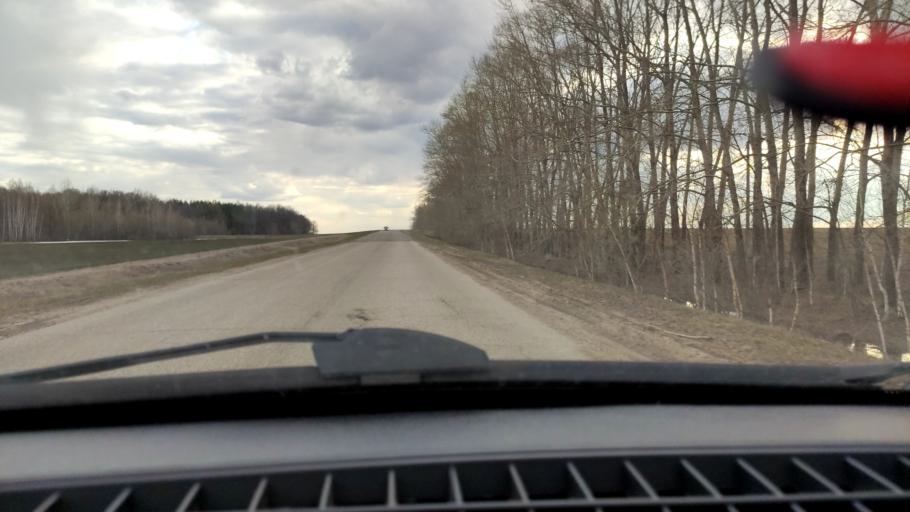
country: RU
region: Bashkortostan
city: Karmaskaly
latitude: 54.3030
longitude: 55.9306
